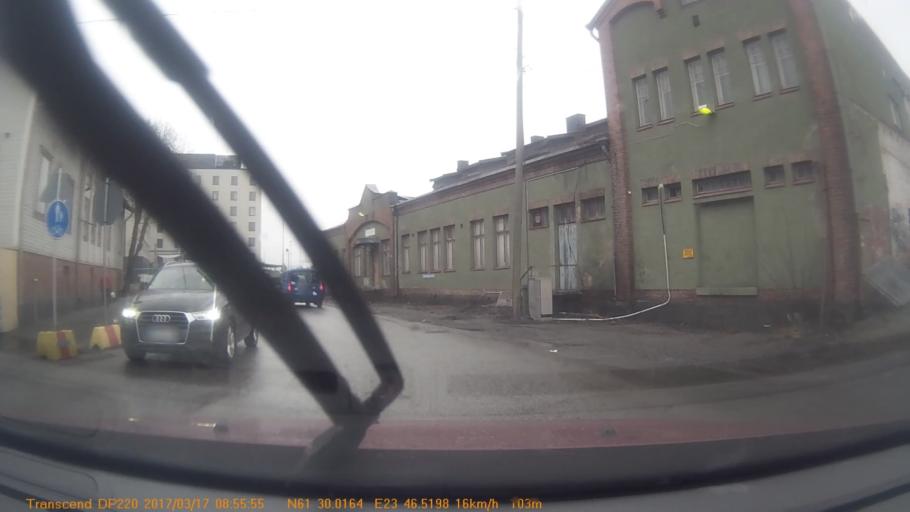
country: FI
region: Pirkanmaa
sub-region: Tampere
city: Tampere
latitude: 61.5003
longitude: 23.7754
